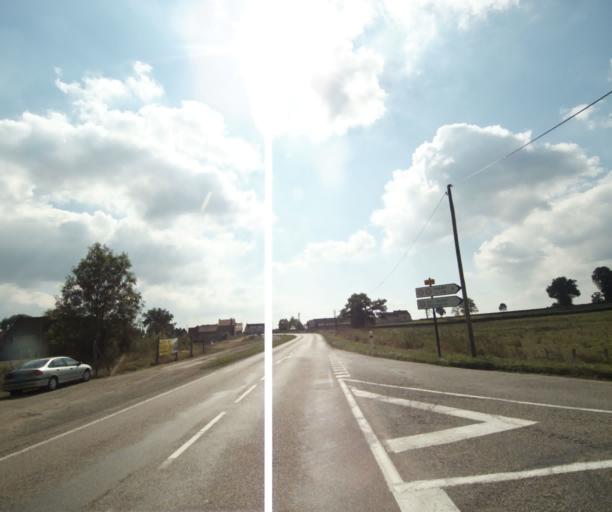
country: FR
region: Bourgogne
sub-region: Departement de Saone-et-Loire
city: Charolles
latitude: 46.3813
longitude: 4.2497
